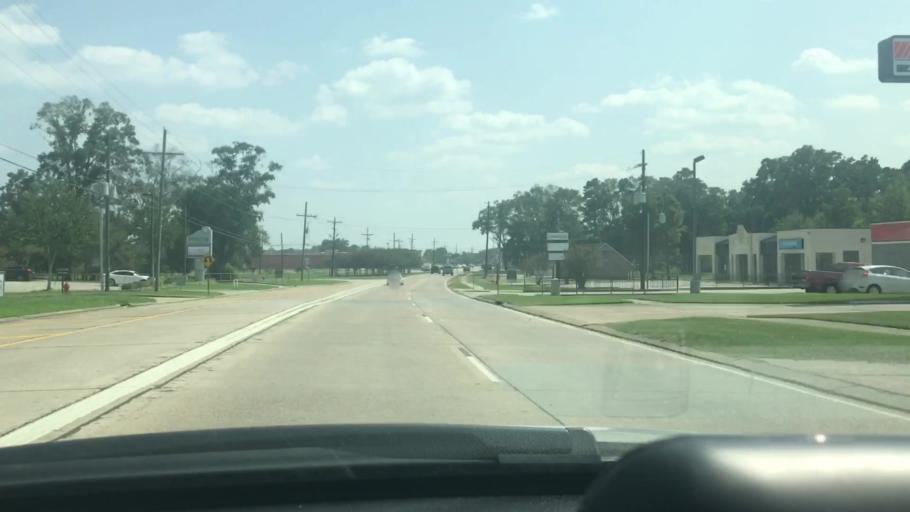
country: US
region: Louisiana
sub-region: Livingston Parish
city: Denham Springs
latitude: 30.4797
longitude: -90.9559
